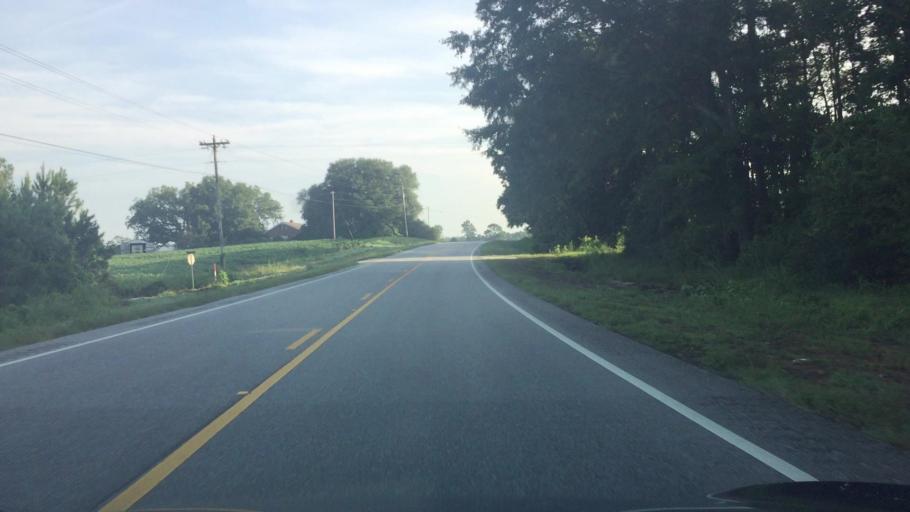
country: US
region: Alabama
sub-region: Covington County
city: Andalusia
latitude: 31.1679
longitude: -86.4602
